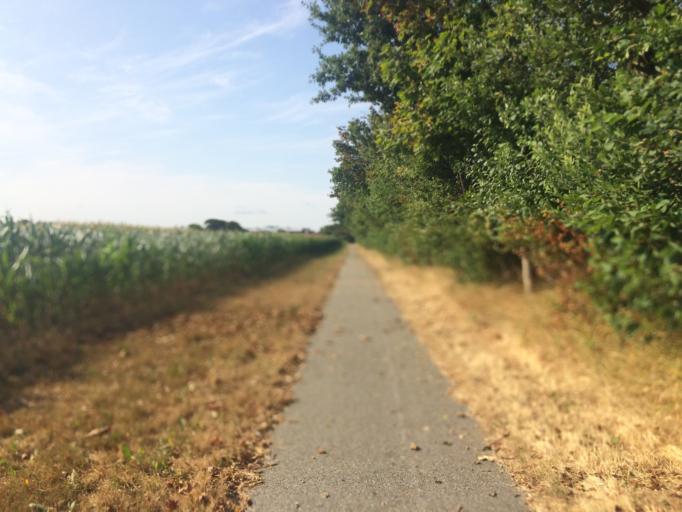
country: DK
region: Central Jutland
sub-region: Holstebro Kommune
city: Vinderup
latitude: 56.6109
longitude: 8.7728
